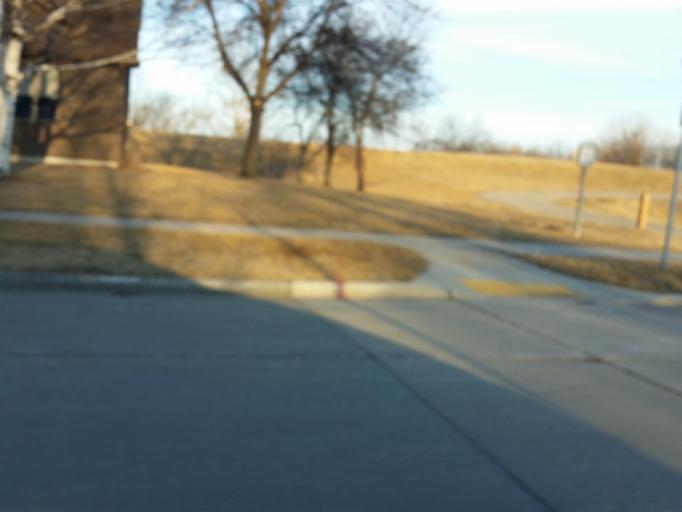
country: US
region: North Dakota
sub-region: Grand Forks County
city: Grand Forks
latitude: 47.8751
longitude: -97.0260
